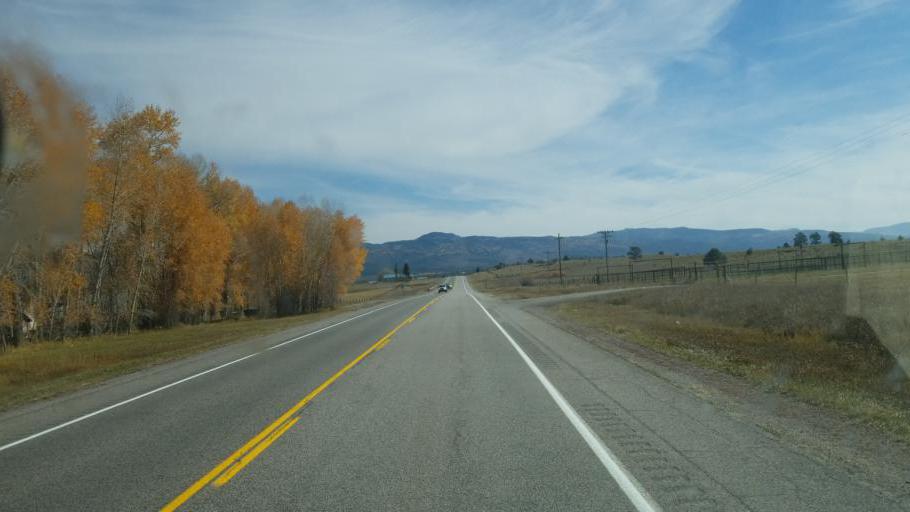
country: US
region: New Mexico
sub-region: Rio Arriba County
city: Chama
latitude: 36.8879
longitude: -106.6241
